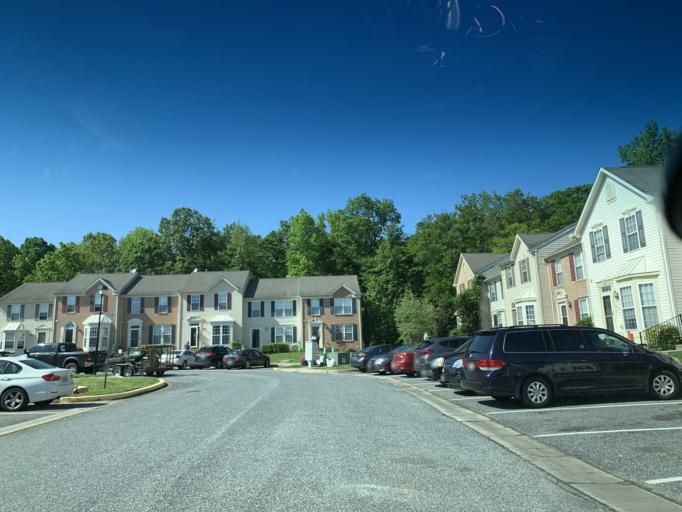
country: US
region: Maryland
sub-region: Harford County
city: Perryman
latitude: 39.4945
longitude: -76.2158
